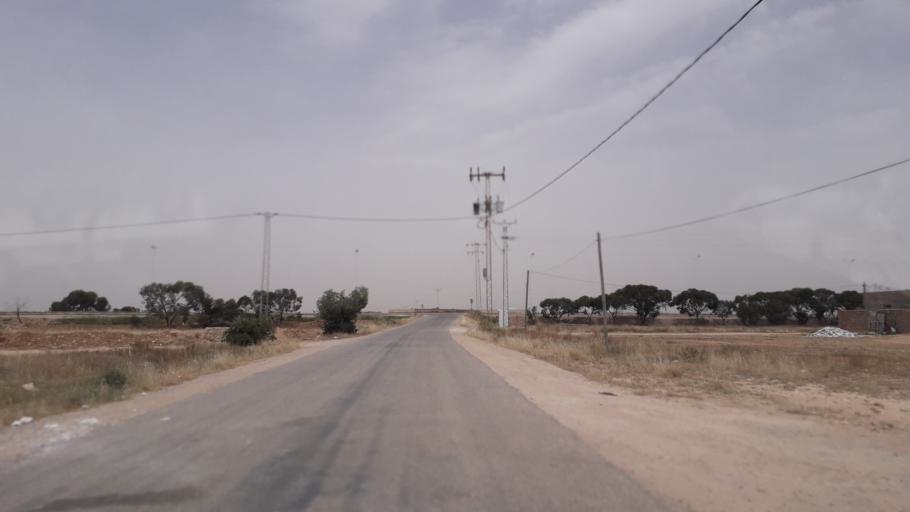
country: TN
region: Safaqis
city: Al Qarmadah
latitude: 34.8493
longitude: 10.7530
